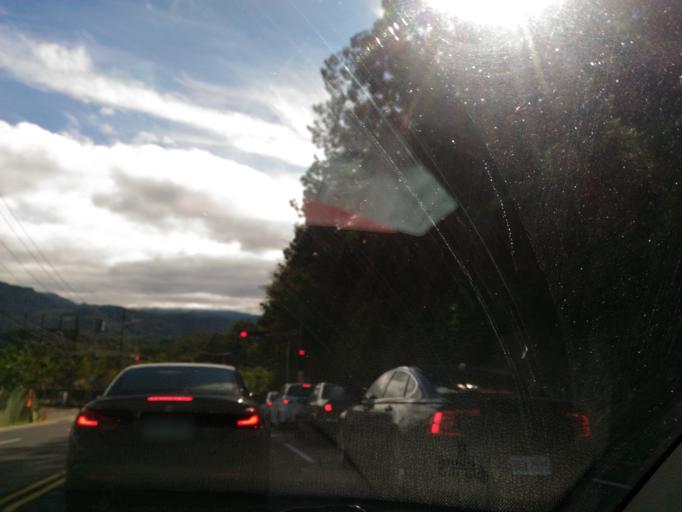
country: TW
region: Taiwan
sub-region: Hsinchu
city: Hsinchu
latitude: 24.7130
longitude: 121.0703
